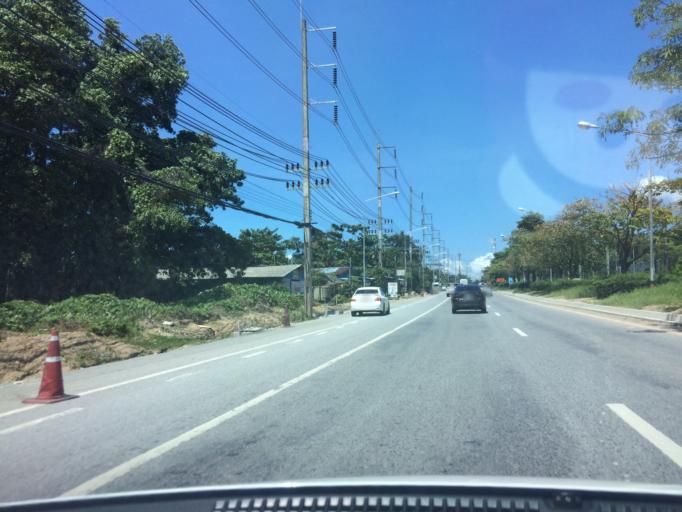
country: TH
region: Phuket
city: Thalang
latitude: 8.0988
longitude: 98.3360
